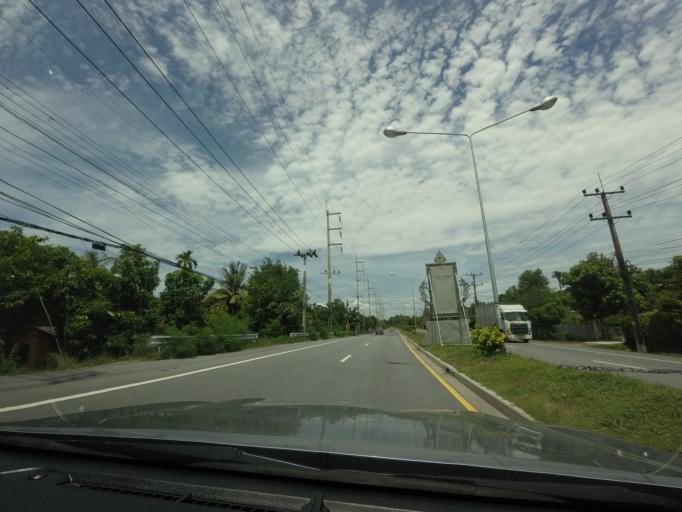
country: TH
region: Songkhla
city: Krasae Sin
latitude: 7.5686
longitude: 100.4107
